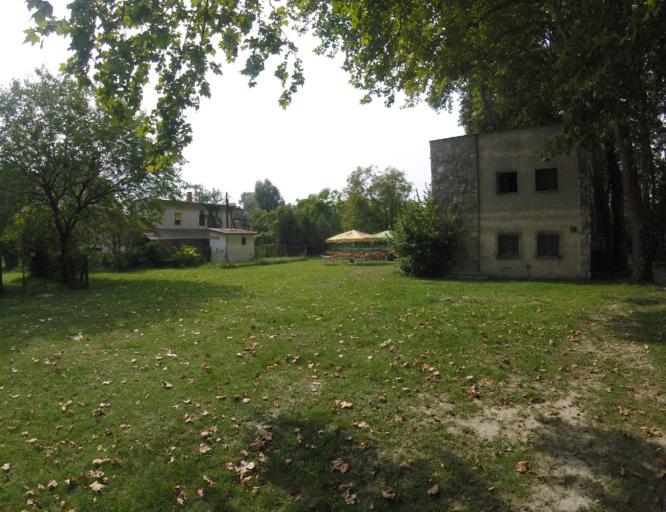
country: HU
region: Pest
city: Budakalasz
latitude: 47.6171
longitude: 19.0863
